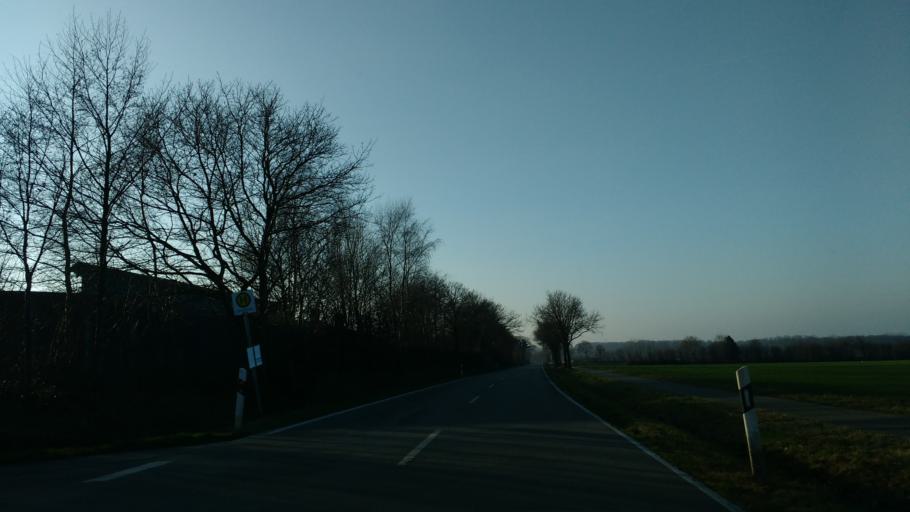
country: DE
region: Schleswig-Holstein
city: Tappendorf
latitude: 54.1073
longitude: 9.6843
